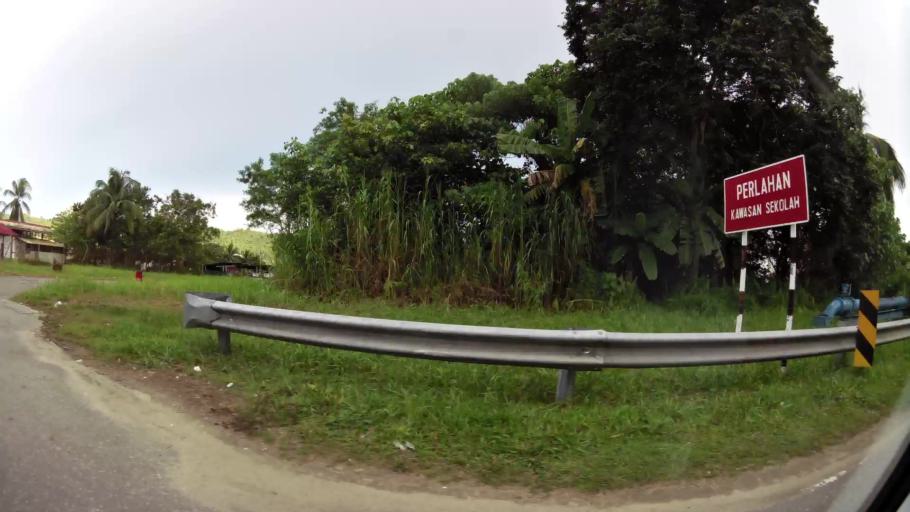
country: BN
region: Brunei and Muara
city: Bandar Seri Begawan
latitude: 4.9018
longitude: 114.9902
